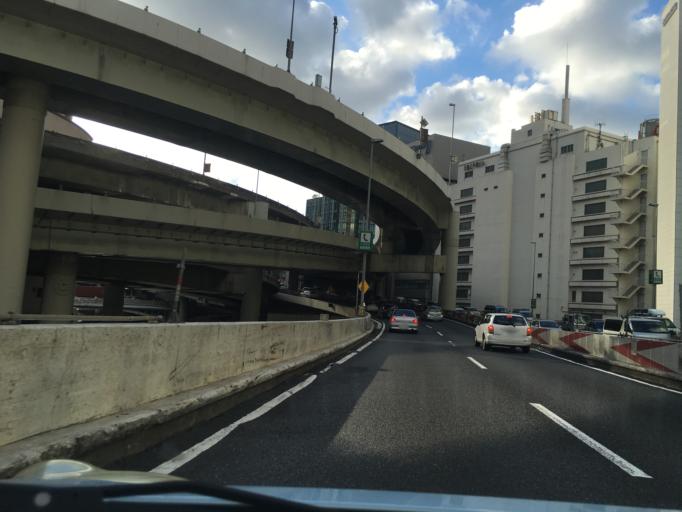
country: JP
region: Tokyo
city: Tokyo
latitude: 35.6840
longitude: 139.7789
